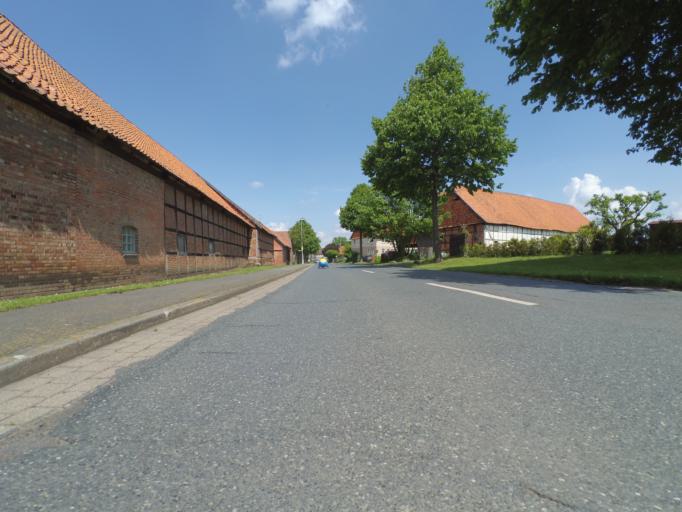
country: DE
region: Lower Saxony
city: Schellerten
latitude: 52.1926
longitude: 10.0332
